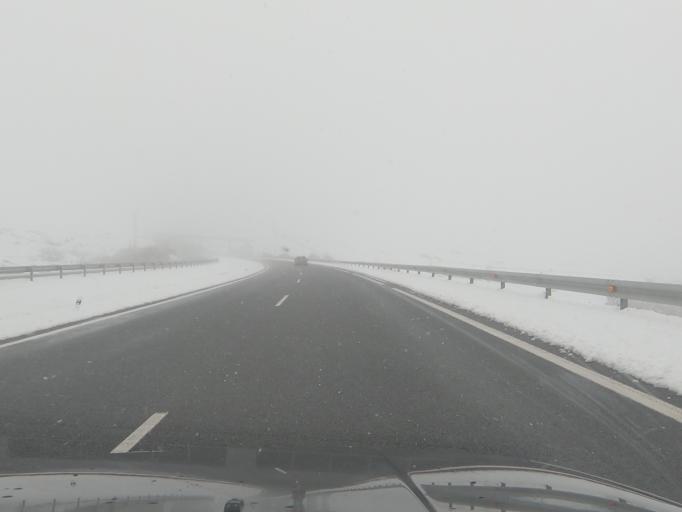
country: ES
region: Castille and Leon
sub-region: Provincia de Zamora
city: Pias
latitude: 42.0480
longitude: -7.0798
